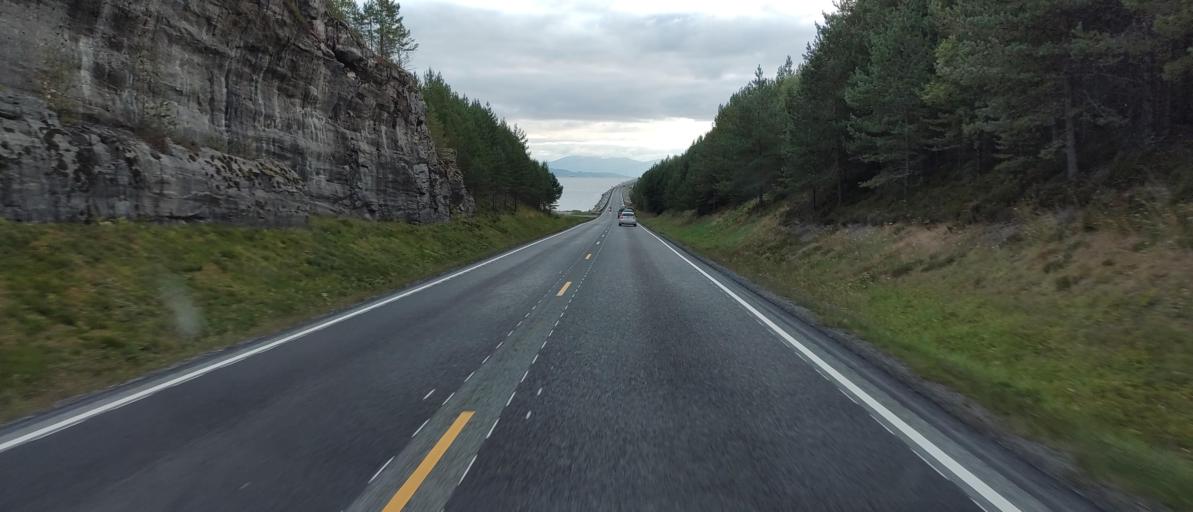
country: NO
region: More og Romsdal
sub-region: Molde
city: Hjelset
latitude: 62.7334
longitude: 7.3747
